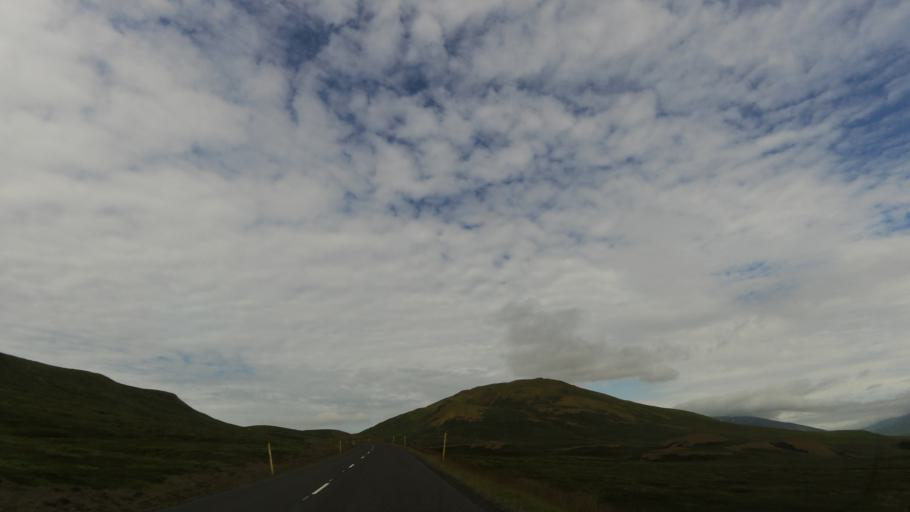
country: IS
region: Northeast
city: Akureyri
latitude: 65.7946
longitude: -17.9384
